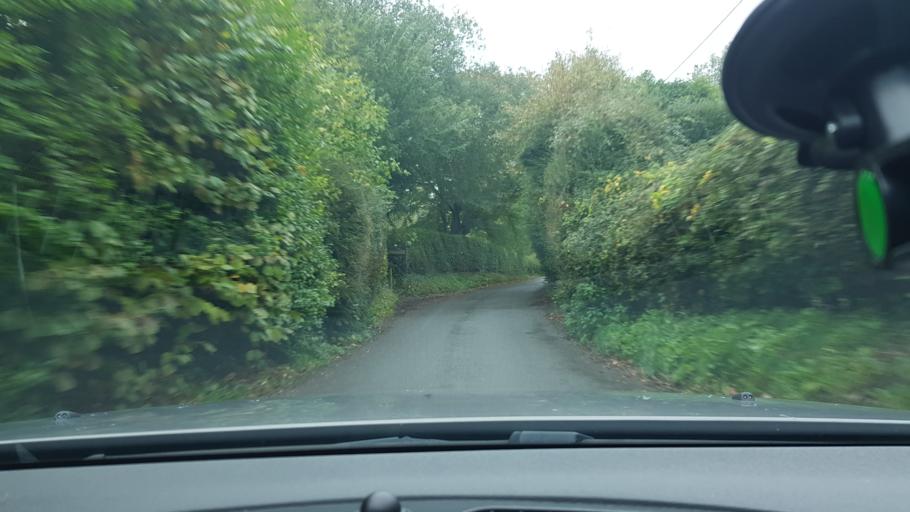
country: GB
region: England
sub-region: Wiltshire
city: Burbage
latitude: 51.3658
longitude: -1.6835
